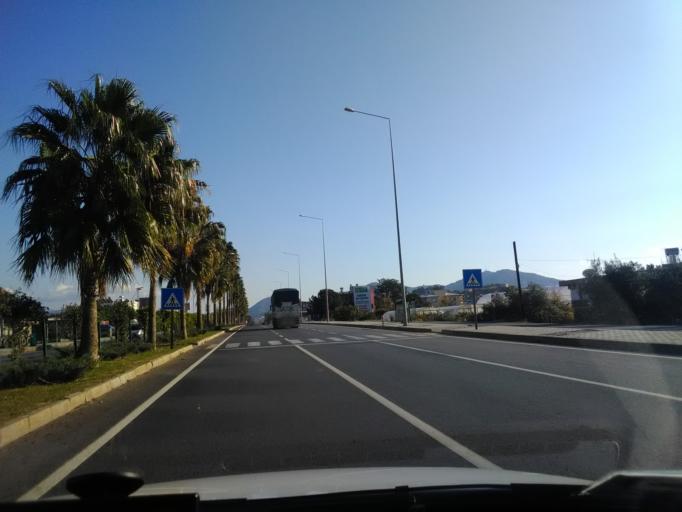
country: TR
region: Antalya
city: Gazipasa
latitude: 36.2853
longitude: 32.2972
